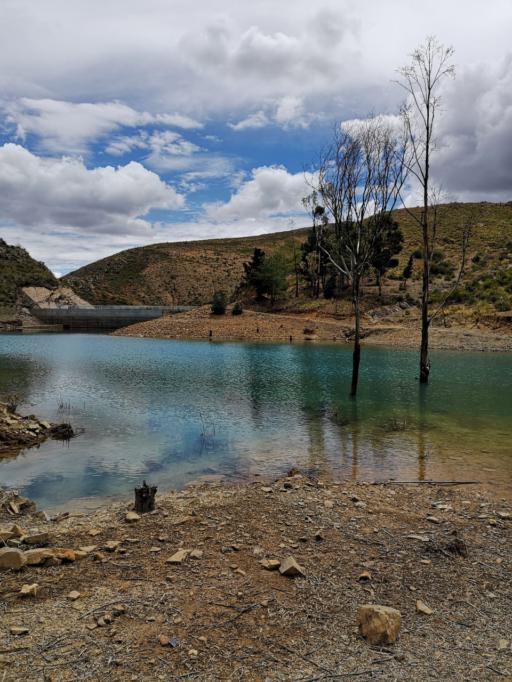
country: BO
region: Cochabamba
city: Tarata
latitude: -17.6584
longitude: -66.1308
